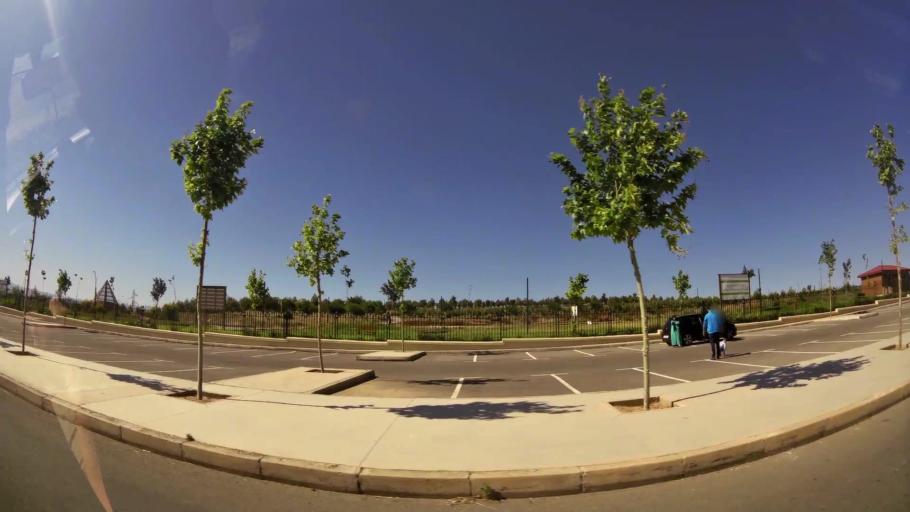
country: MA
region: Oriental
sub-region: Oujda-Angad
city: Oujda
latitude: 34.7375
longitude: -1.9258
